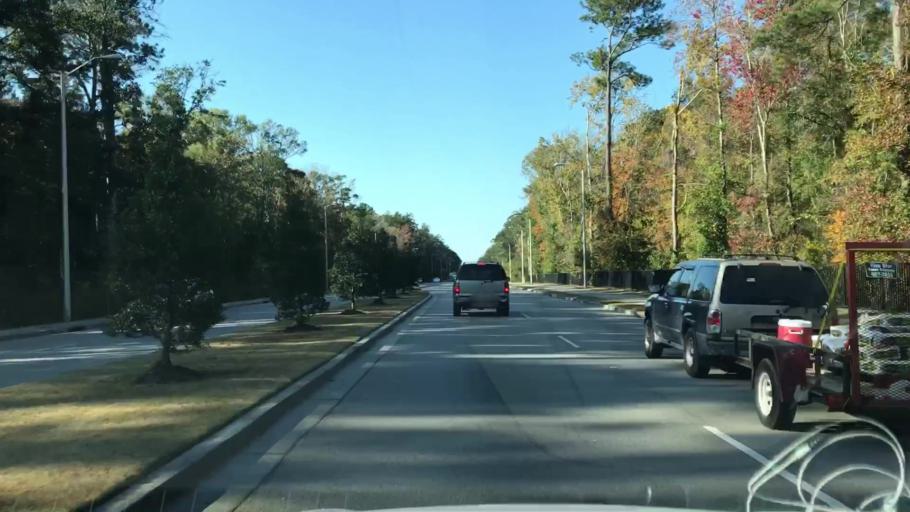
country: US
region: South Carolina
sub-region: Charleston County
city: Shell Point
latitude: 32.8205
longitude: -80.0910
